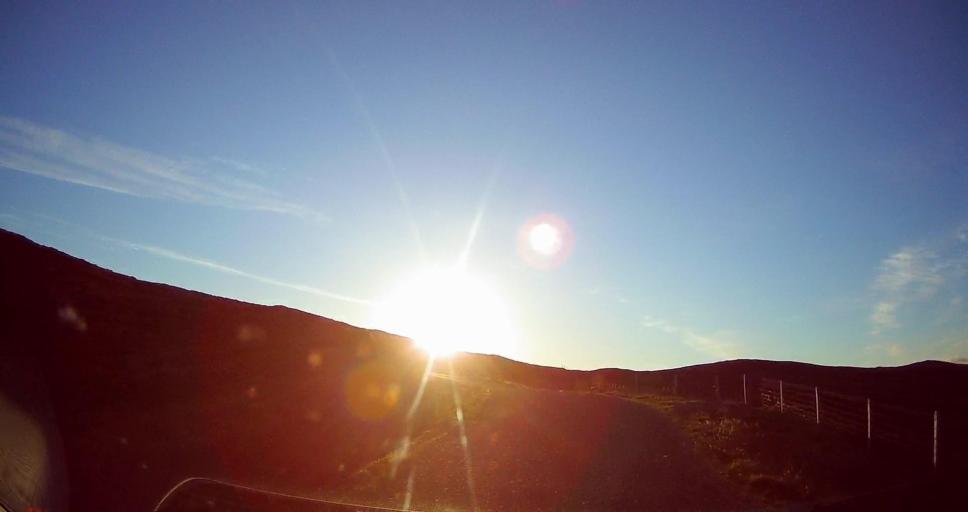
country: GB
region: Scotland
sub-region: Shetland Islands
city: Lerwick
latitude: 60.4400
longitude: -1.3987
